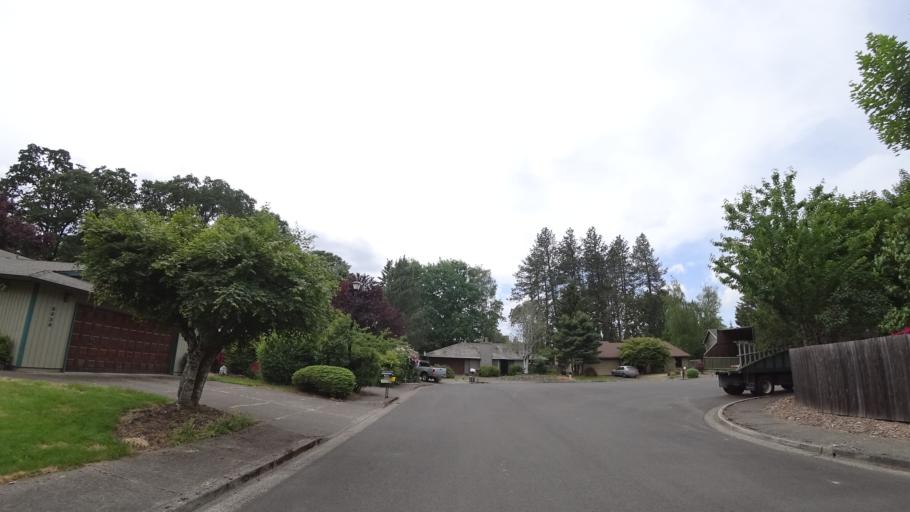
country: US
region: Oregon
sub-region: Washington County
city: Metzger
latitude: 45.4544
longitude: -122.7677
